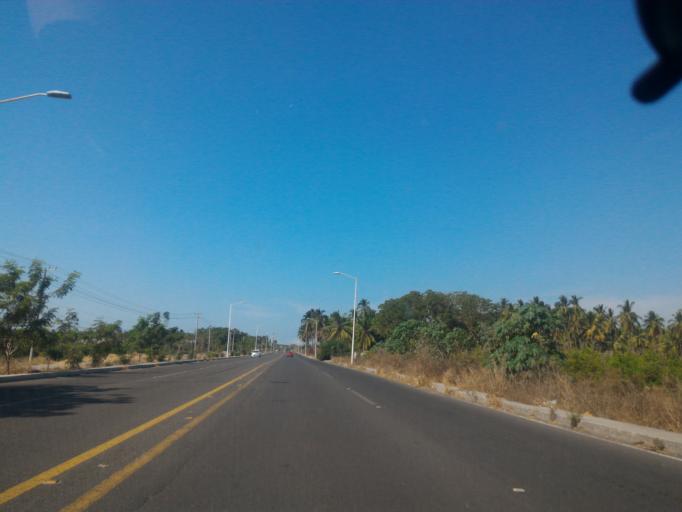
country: MX
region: Colima
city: Tecoman
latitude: 18.9061
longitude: -103.8963
